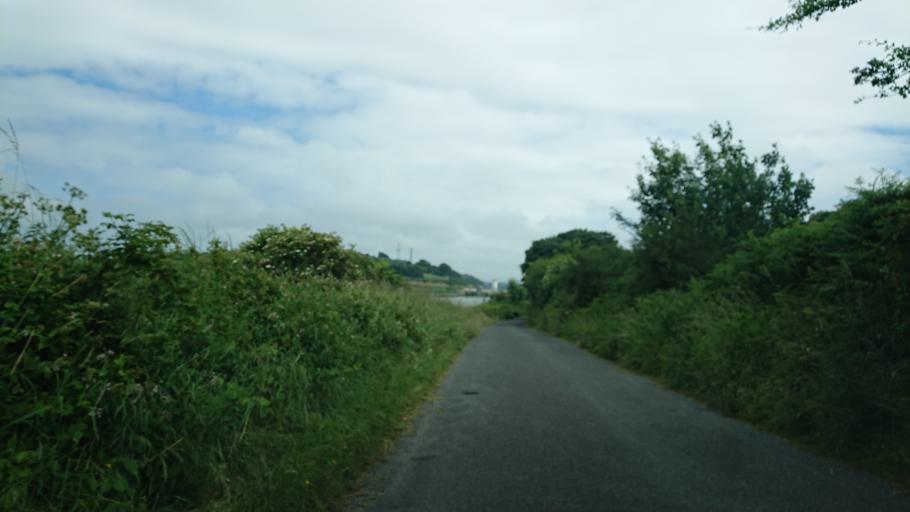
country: IE
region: Munster
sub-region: Waterford
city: Waterford
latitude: 52.2715
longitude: -7.1417
